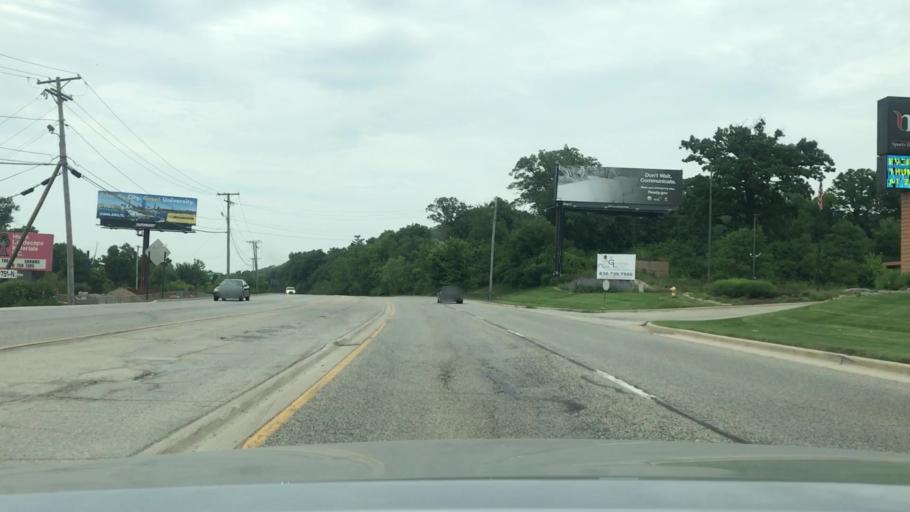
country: US
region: Illinois
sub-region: Will County
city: Bolingbrook
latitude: 41.7212
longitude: -88.0662
